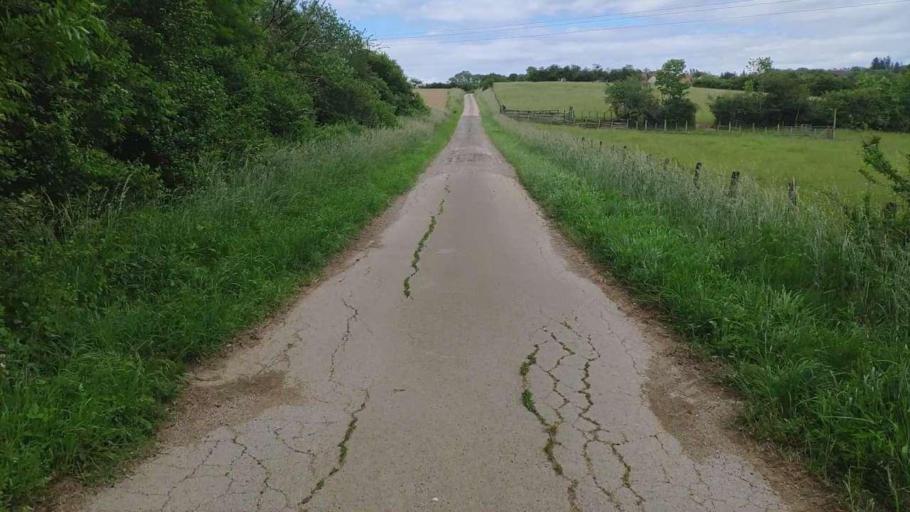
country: FR
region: Franche-Comte
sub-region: Departement du Jura
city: Bletterans
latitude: 46.7893
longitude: 5.5506
